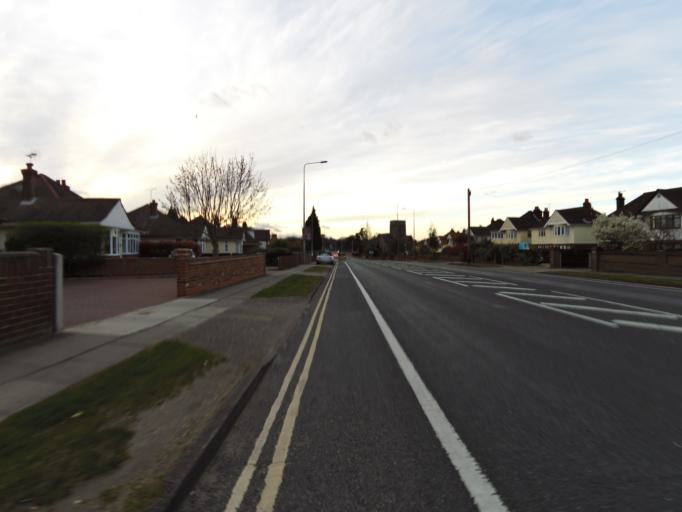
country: GB
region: England
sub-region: Suffolk
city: Kesgrave
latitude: 52.0398
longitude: 1.1998
